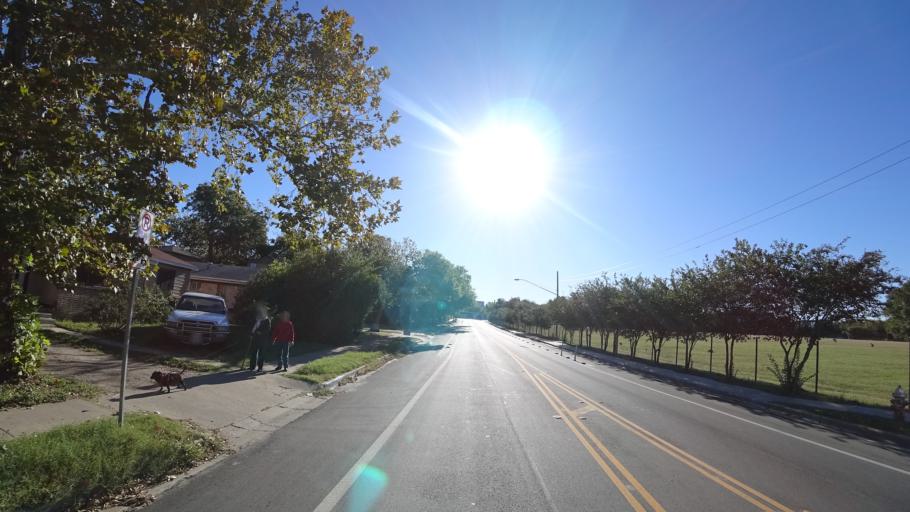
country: US
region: Texas
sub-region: Travis County
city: Austin
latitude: 30.3184
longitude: -97.7238
